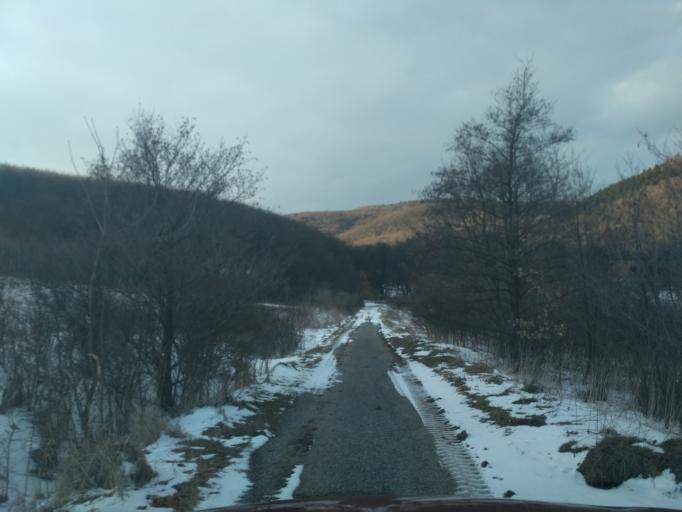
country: SK
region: Kosicky
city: Kosice
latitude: 48.7441
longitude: 21.1506
